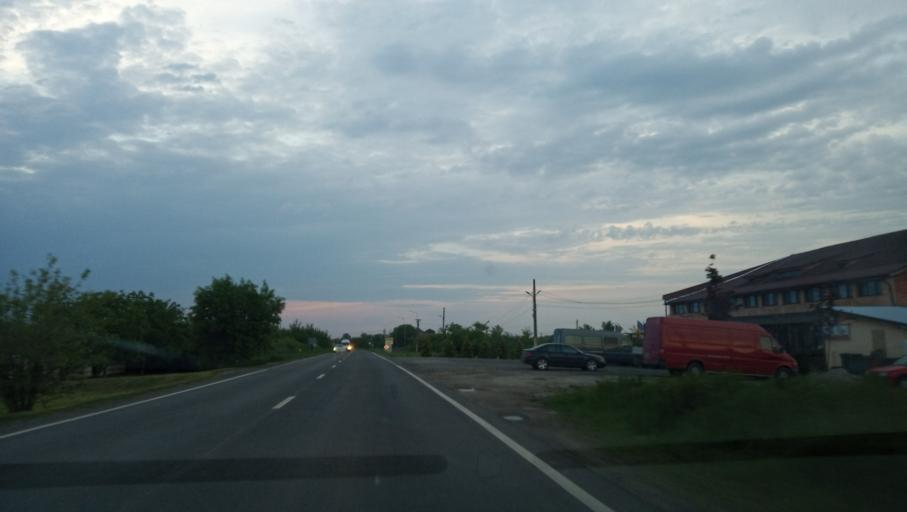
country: RO
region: Timis
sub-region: Comuna Jebel
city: Jebel
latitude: 45.5503
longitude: 21.2229
